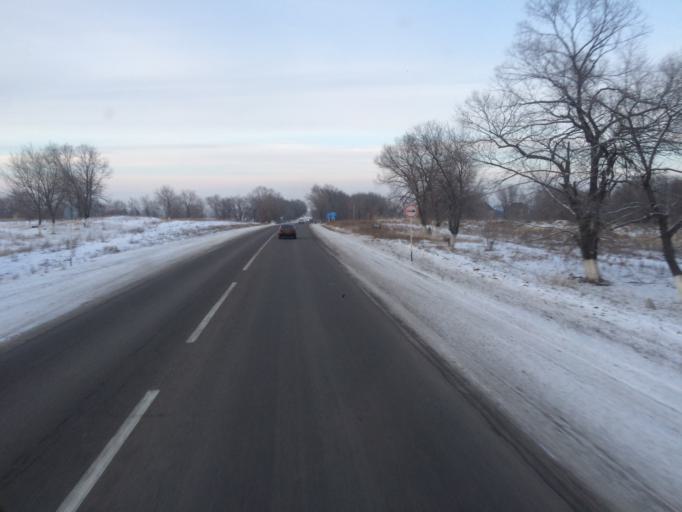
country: KZ
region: Almaty Oblysy
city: Burunday
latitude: 43.3248
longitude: 76.6628
